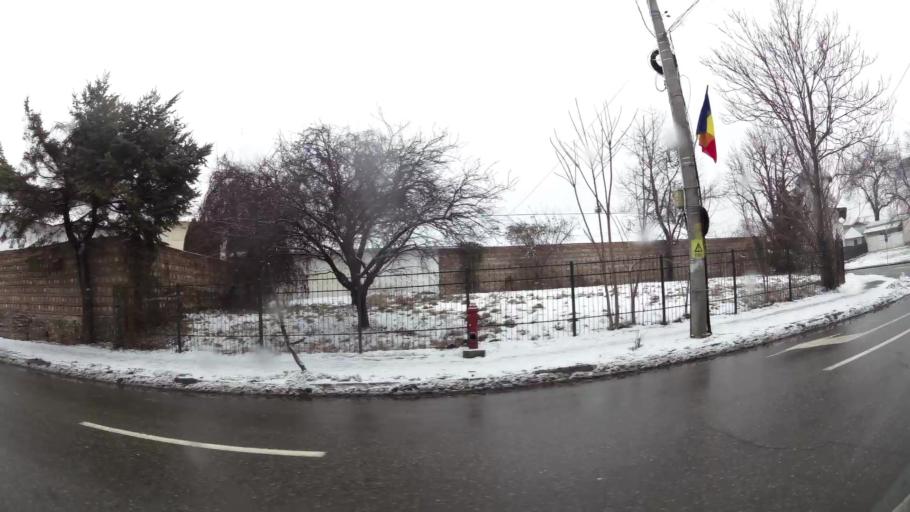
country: RO
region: Dambovita
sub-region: Municipiul Targoviste
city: Targoviste
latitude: 44.9294
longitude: 25.4620
